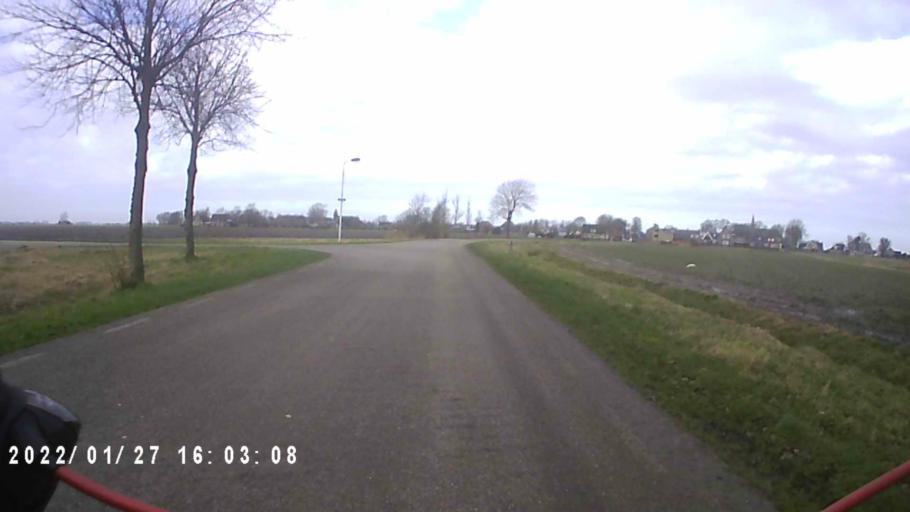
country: NL
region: Friesland
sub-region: Gemeente Dongeradeel
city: Anjum
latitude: 53.3767
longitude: 6.0891
